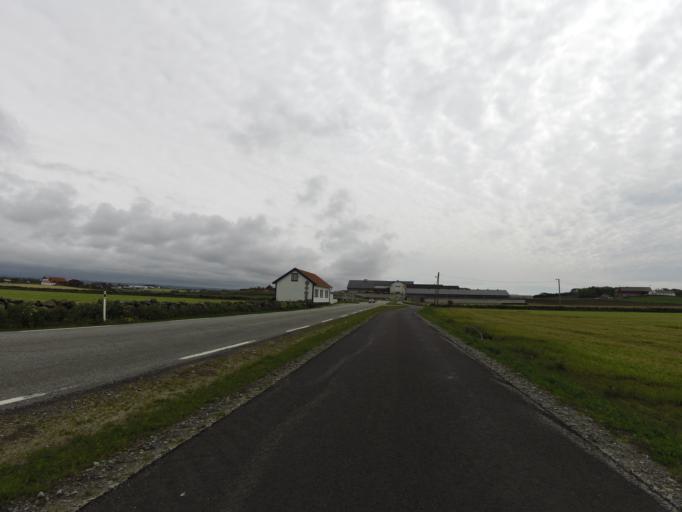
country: NO
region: Rogaland
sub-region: Ha
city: Naerbo
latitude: 58.6820
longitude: 5.5655
